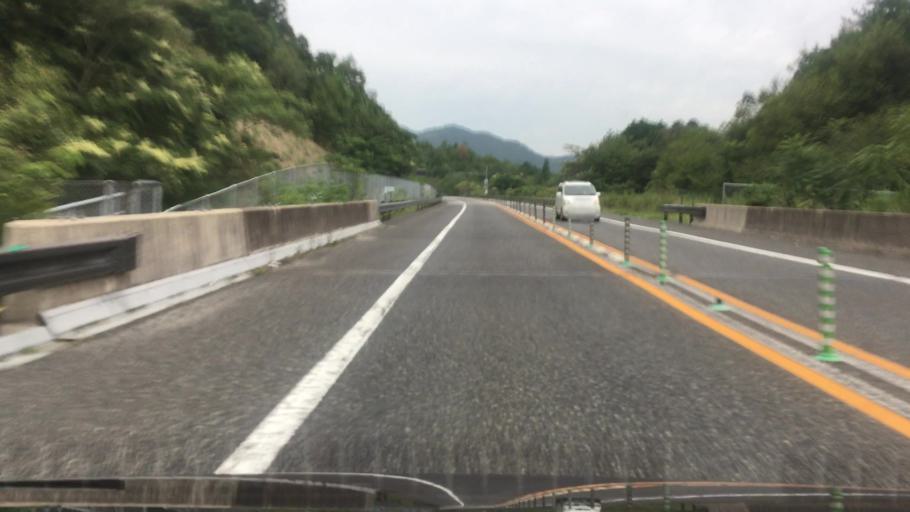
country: JP
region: Kyoto
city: Fukuchiyama
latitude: 35.1648
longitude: 135.0844
